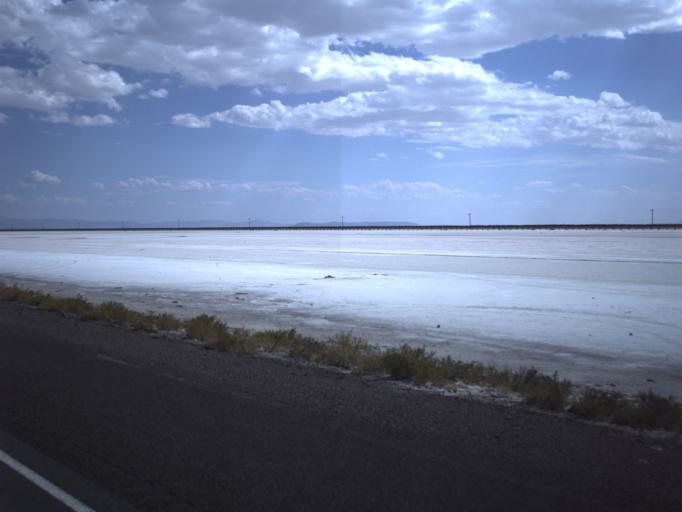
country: US
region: Utah
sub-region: Tooele County
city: Wendover
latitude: 40.7358
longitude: -113.7216
